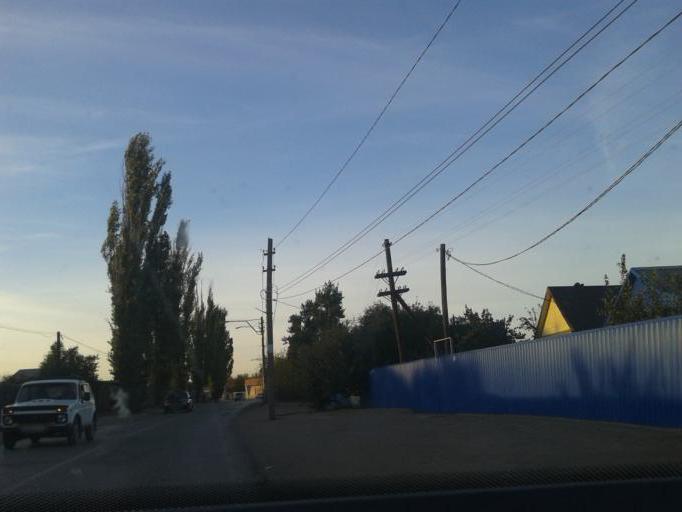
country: RU
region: Volgograd
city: Krasnoslobodsk
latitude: 48.7075
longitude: 44.5805
